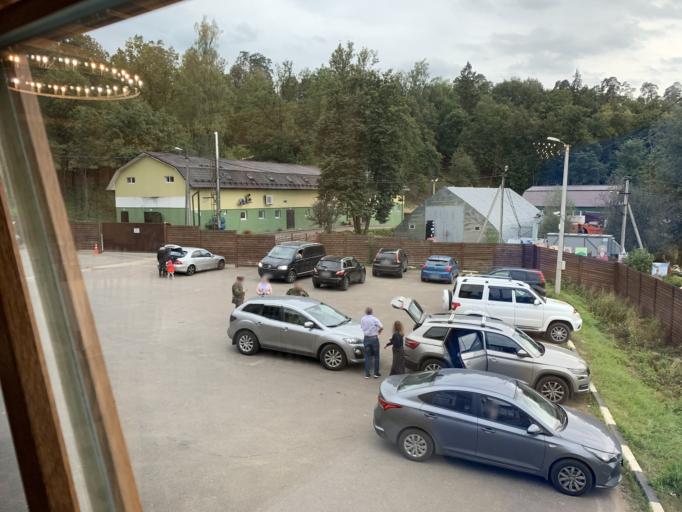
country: RU
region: Moskovskaya
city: Zvenigorod
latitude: 55.7351
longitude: 36.8108
